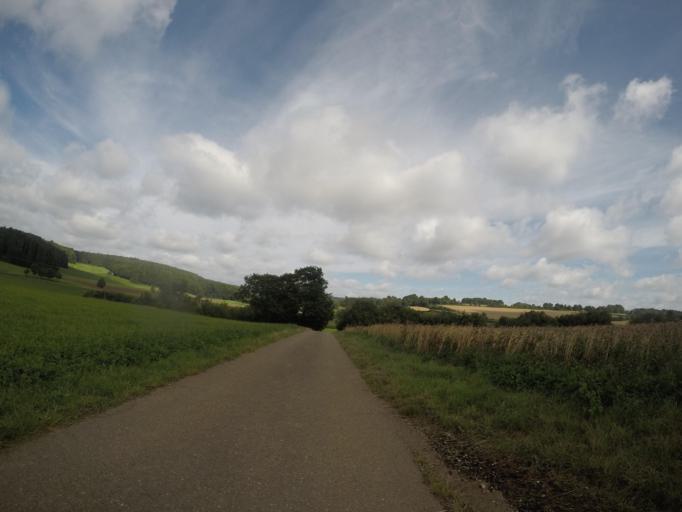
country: DE
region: Baden-Wuerttemberg
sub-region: Tuebingen Region
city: Westerheim
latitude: 48.4582
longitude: 9.6333
